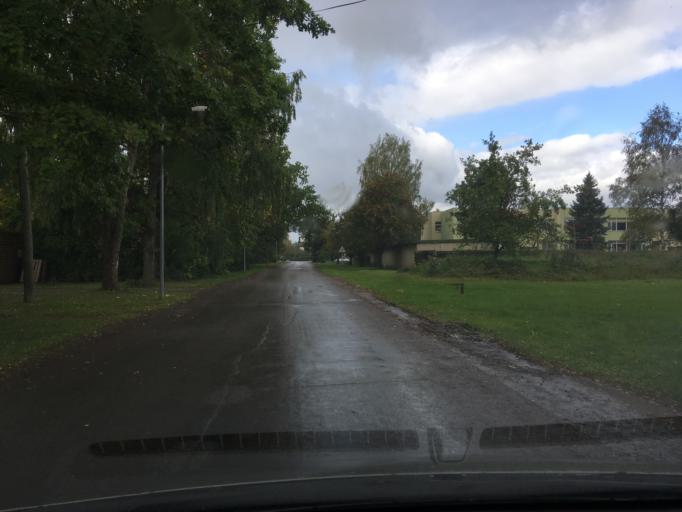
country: EE
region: Raplamaa
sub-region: Rapla vald
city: Rapla
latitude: 58.9931
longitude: 24.8194
